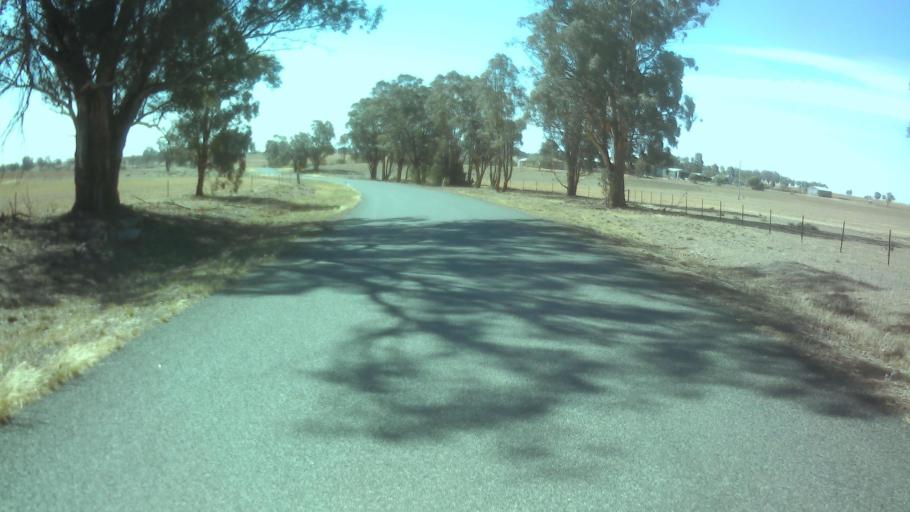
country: AU
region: New South Wales
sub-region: Weddin
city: Grenfell
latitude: -33.7644
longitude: 147.8640
